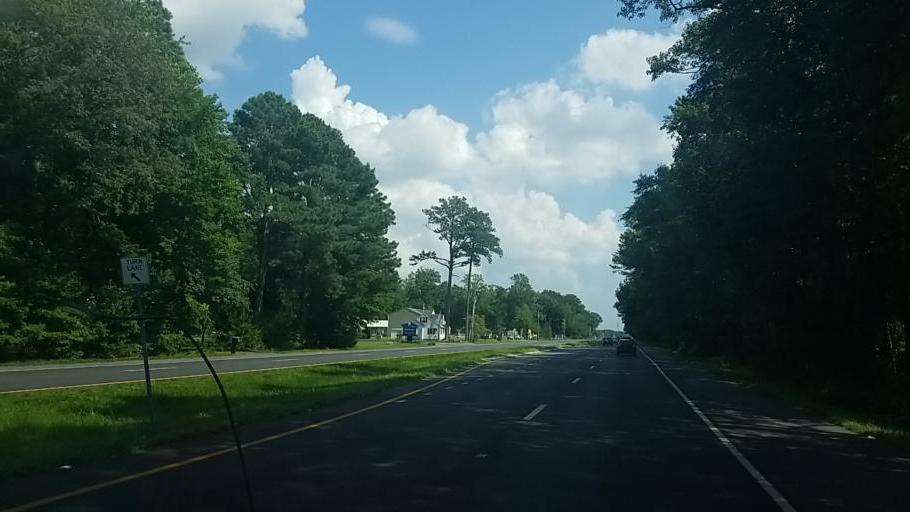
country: US
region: Delaware
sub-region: Sussex County
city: Millsboro
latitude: 38.5544
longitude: -75.2682
